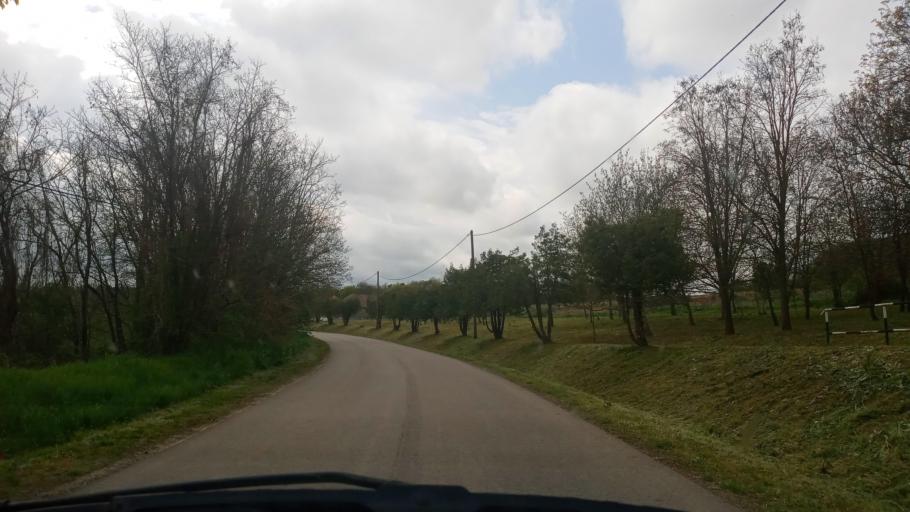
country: HU
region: Baranya
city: Boly
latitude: 45.9799
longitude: 18.4233
